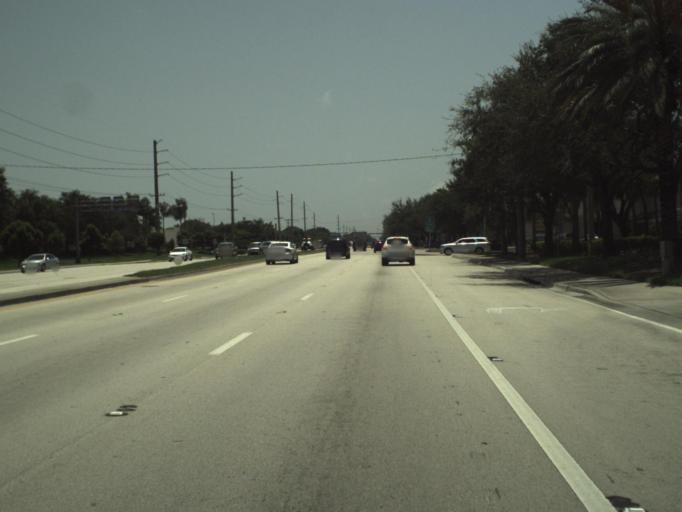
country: US
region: Florida
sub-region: Broward County
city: Coconut Creek
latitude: 26.2305
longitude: -80.1569
